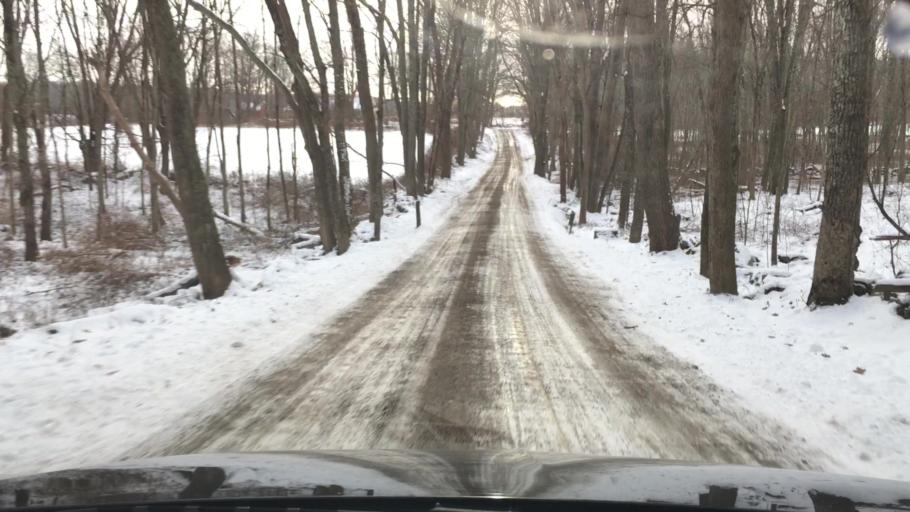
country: US
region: Connecticut
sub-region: Tolland County
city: Storrs
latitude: 41.8522
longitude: -72.1964
